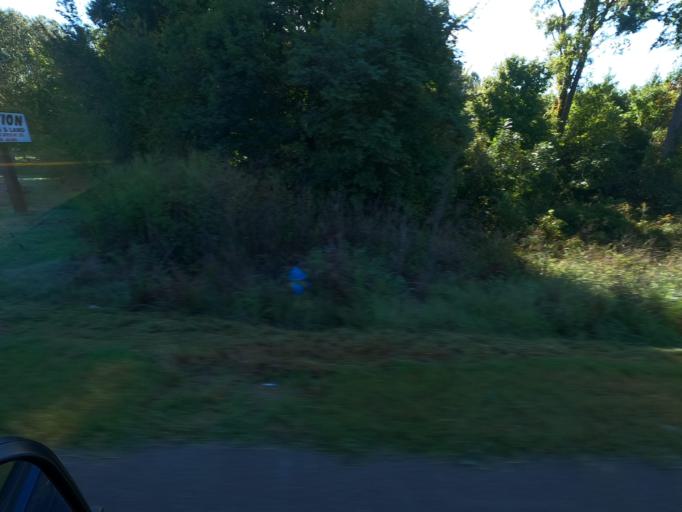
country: US
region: Tennessee
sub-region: Tipton County
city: Atoka
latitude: 35.4530
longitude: -89.7773
